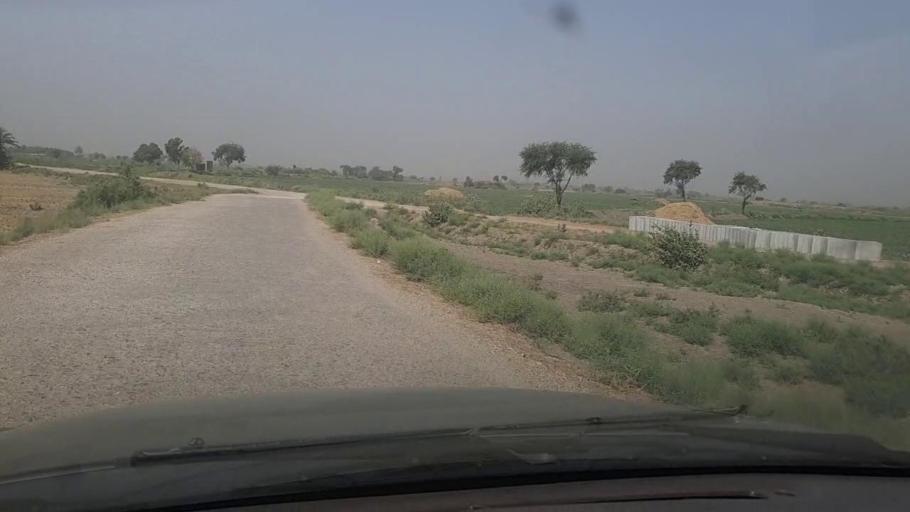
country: PK
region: Sindh
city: Garhi Yasin
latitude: 27.8555
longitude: 68.5445
